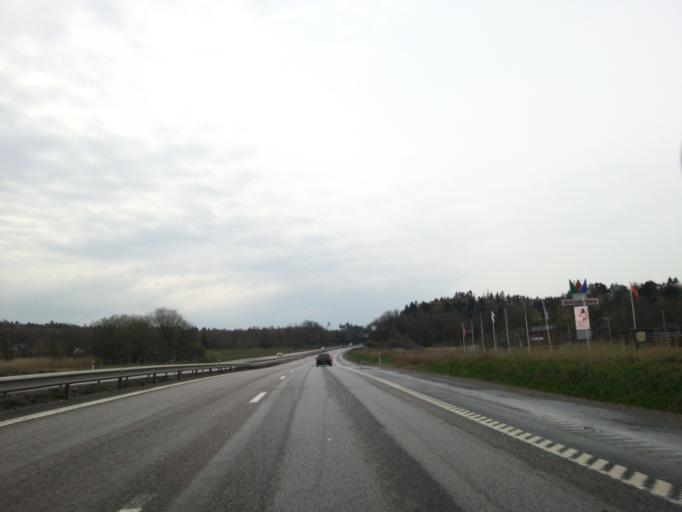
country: SE
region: Halland
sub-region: Kungsbacka Kommun
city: Kungsbacka
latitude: 57.5053
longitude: 12.0527
